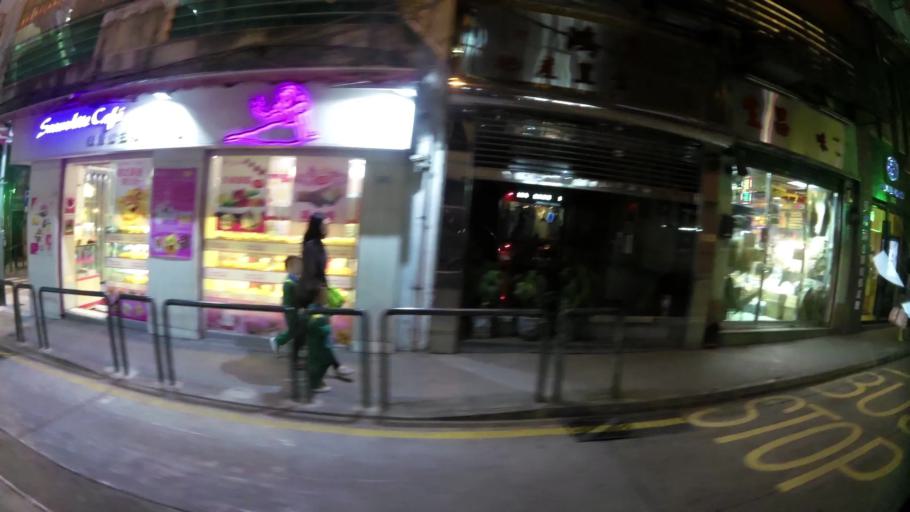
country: MO
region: Macau
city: Macau
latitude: 22.2004
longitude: 113.5452
